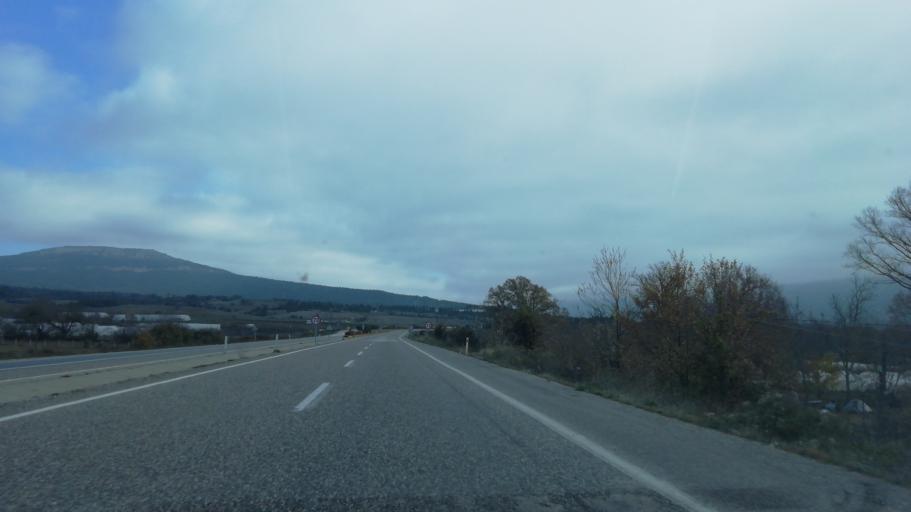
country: TR
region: Karabuk
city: Safranbolu
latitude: 41.2233
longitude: 32.7769
